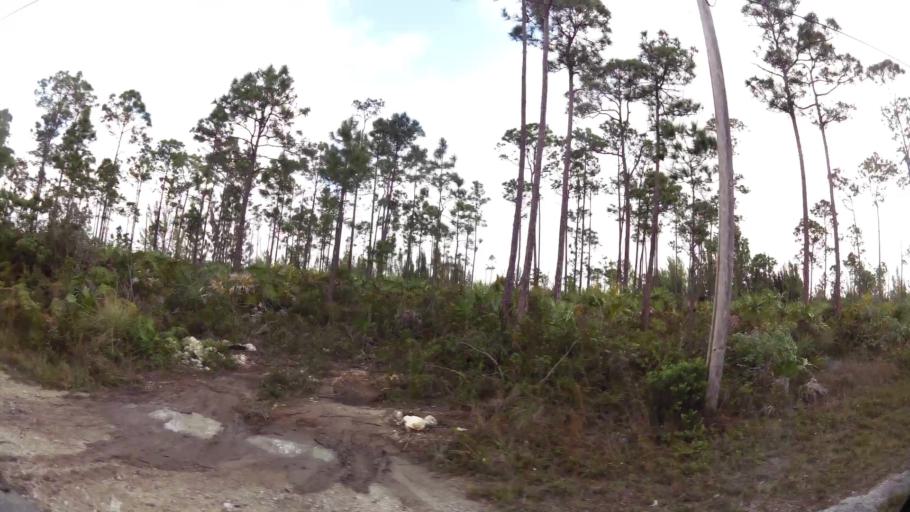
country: BS
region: Freeport
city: Lucaya
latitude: 26.5719
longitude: -78.5824
